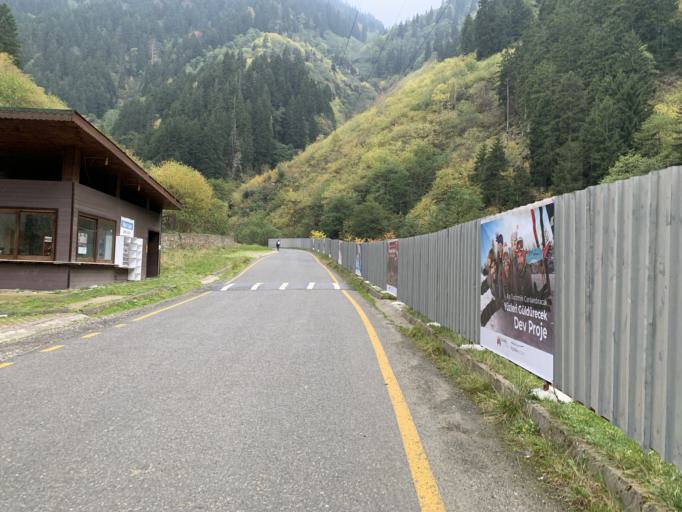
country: TR
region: Trabzon
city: Uzungol
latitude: 40.5946
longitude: 40.3209
